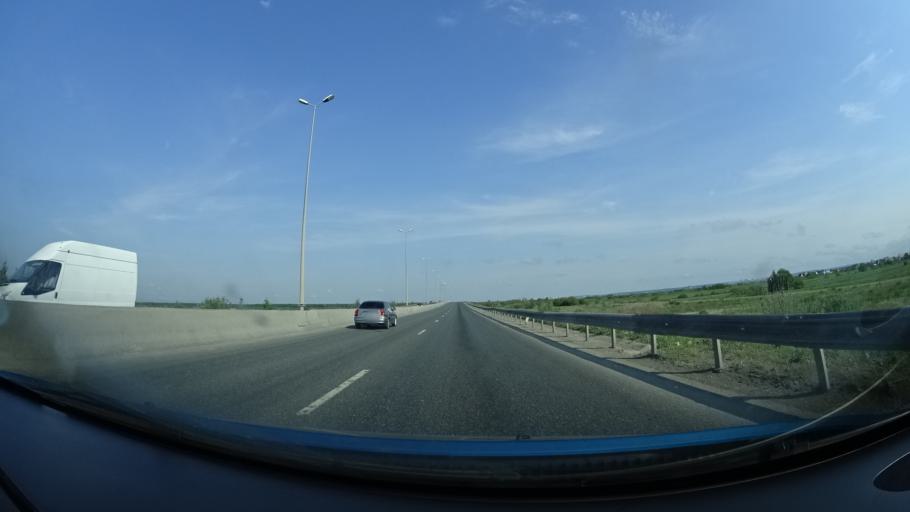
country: RU
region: Perm
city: Kondratovo
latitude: 57.9736
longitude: 56.0886
